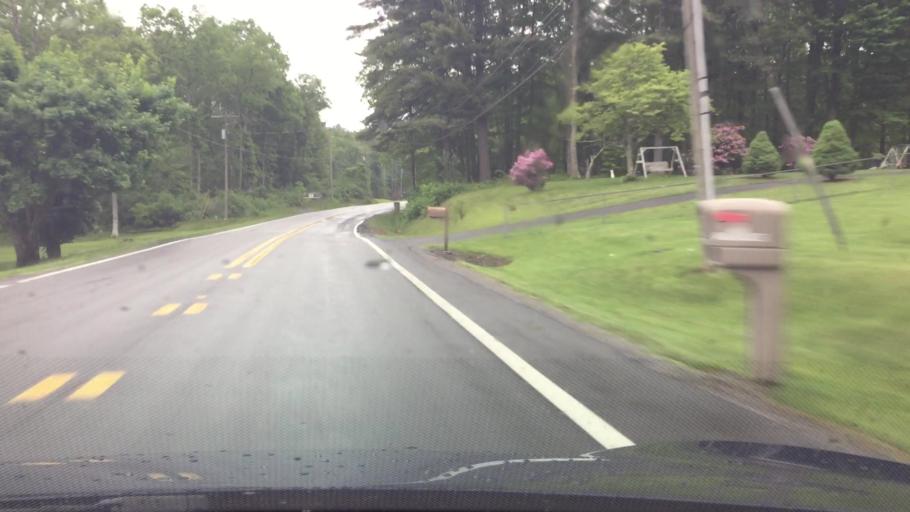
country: US
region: West Virginia
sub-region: Raleigh County
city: Shady Spring
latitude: 37.6906
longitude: -81.0626
